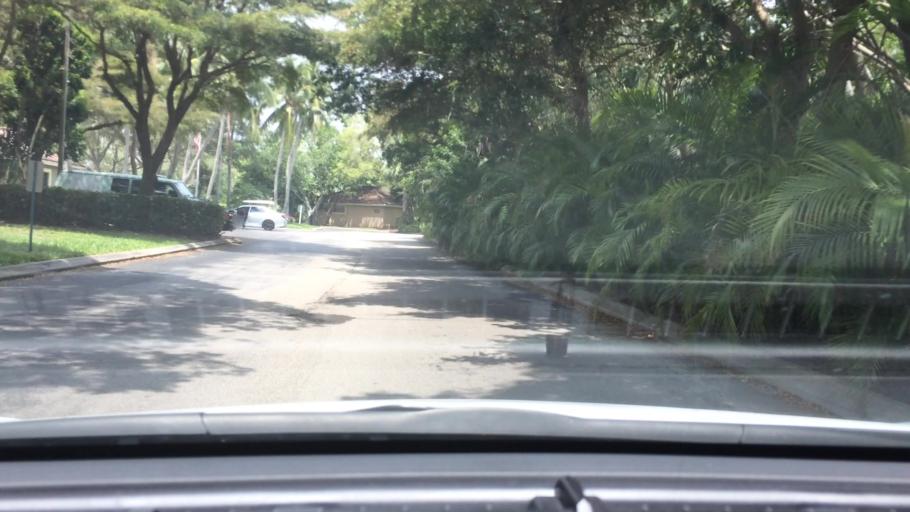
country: US
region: Florida
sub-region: Palm Beach County
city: Boynton Beach
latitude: 26.5219
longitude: -80.1262
